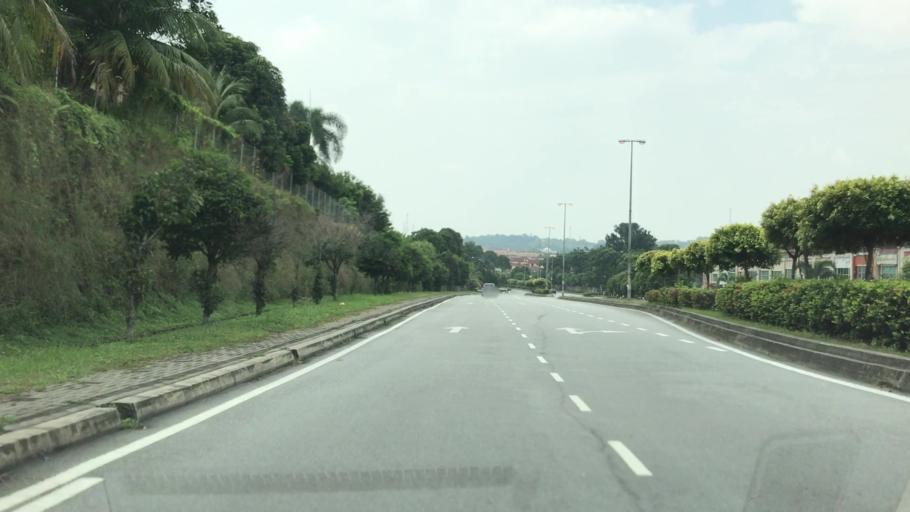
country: MY
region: Putrajaya
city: Putrajaya
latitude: 2.9875
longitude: 101.6647
